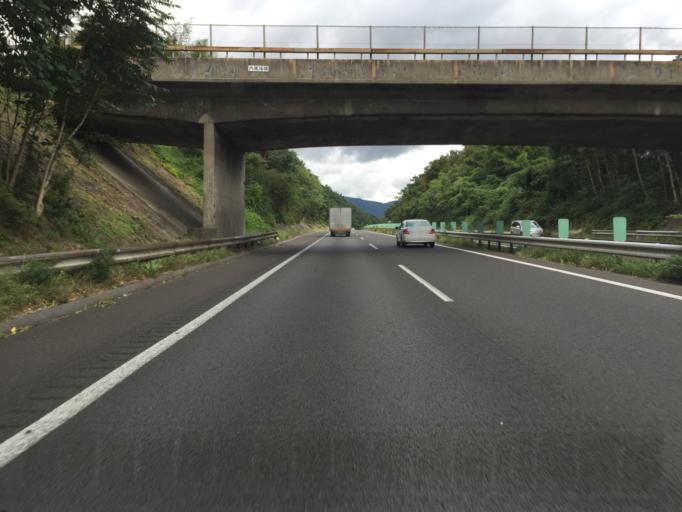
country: JP
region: Fukushima
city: Hobaramachi
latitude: 37.8576
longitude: 140.5137
